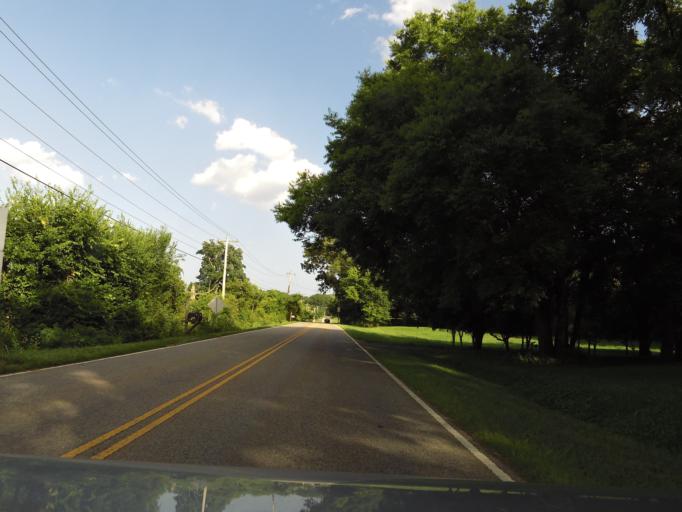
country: US
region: Tennessee
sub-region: Blount County
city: Eagleton Village
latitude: 35.8100
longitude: -83.9158
